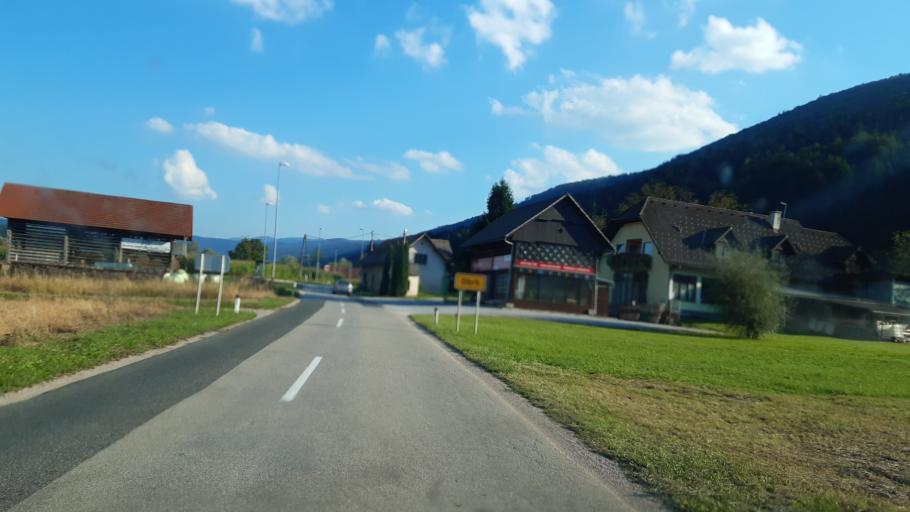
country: SI
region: Dolenjske Toplice
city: Dolenjske Toplice
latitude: 45.7522
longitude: 15.0349
